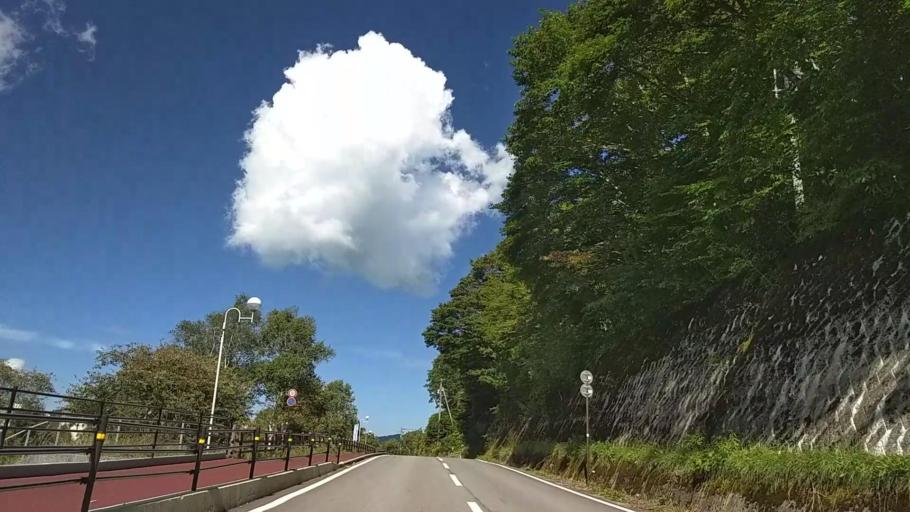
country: JP
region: Nagano
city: Chino
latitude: 36.1016
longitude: 138.2303
